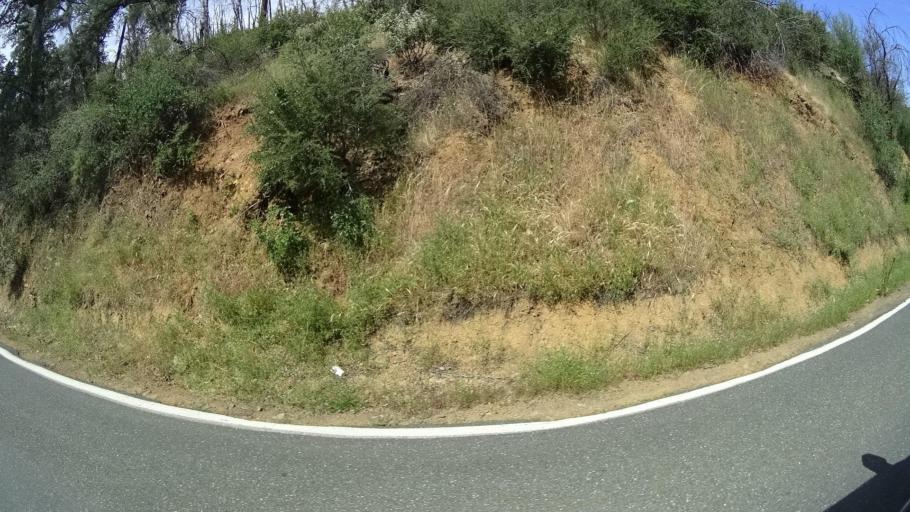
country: US
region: California
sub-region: Lake County
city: Lower Lake
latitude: 38.8860
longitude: -122.6645
